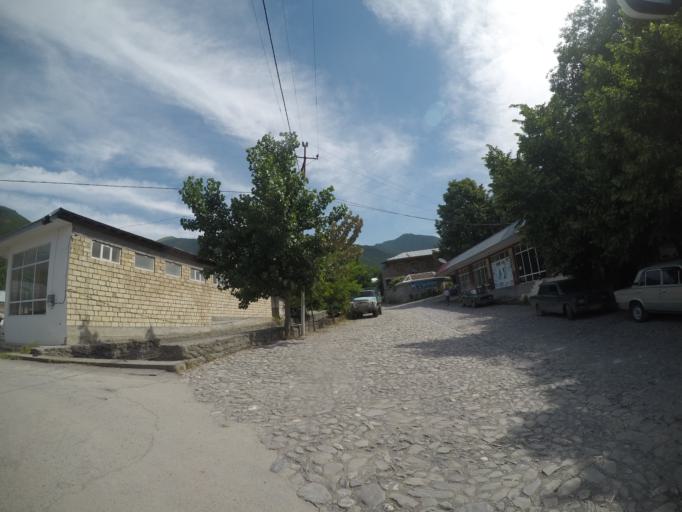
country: AZ
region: Shaki City
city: Sheki
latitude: 41.2480
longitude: 47.1892
